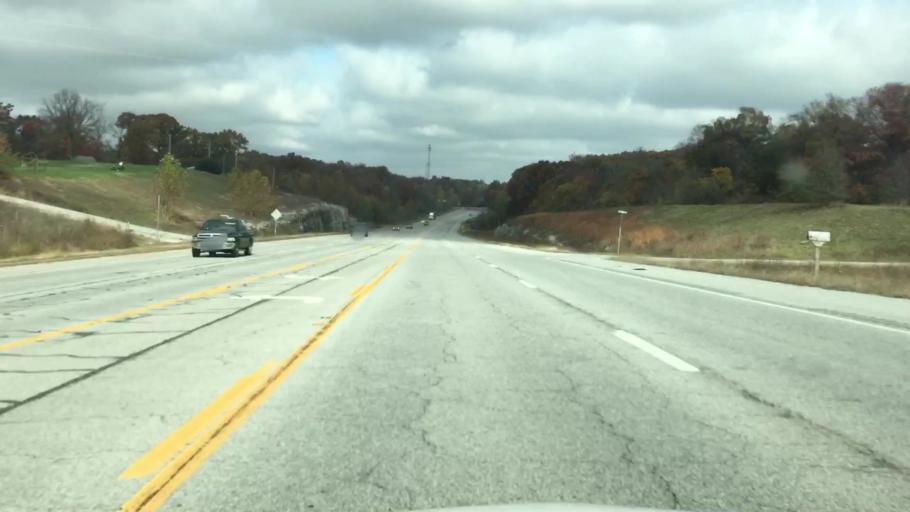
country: US
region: Arkansas
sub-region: Benton County
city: Gentry
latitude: 36.2383
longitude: -94.4875
